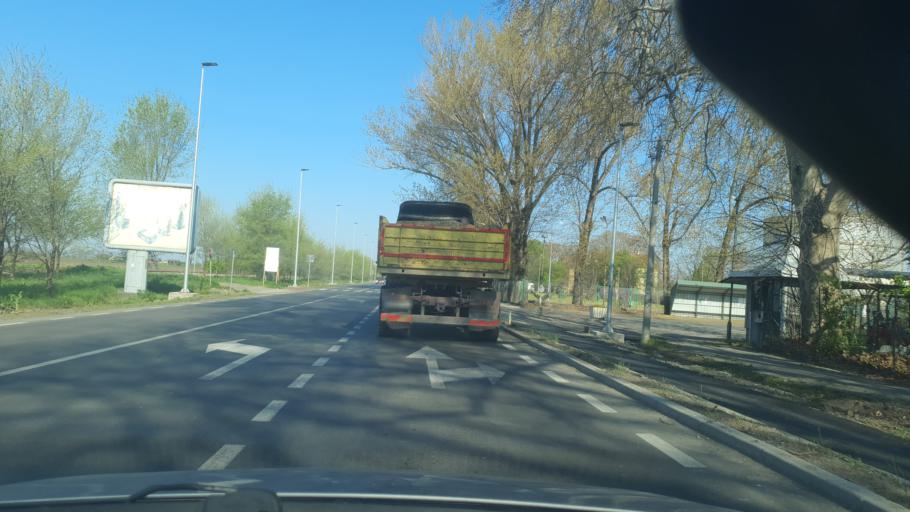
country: RS
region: Autonomna Pokrajina Vojvodina
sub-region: Juznobacki Okrug
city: Vrbas
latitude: 45.5884
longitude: 19.5998
